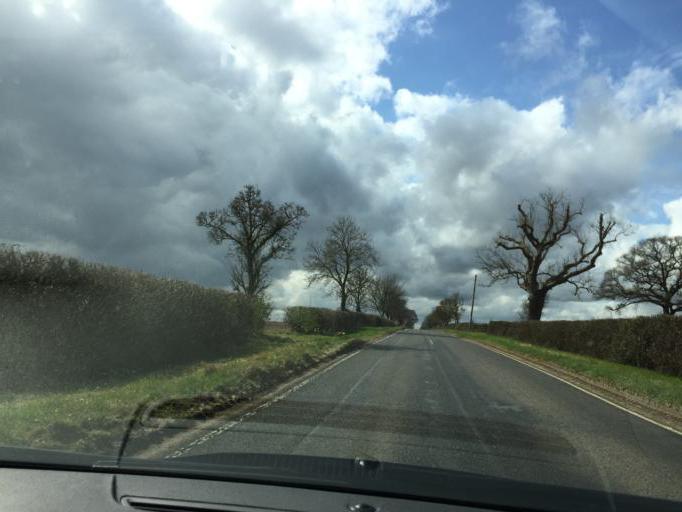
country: GB
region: England
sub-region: Oxfordshire
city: Stonesfield
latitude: 51.8611
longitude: -1.4038
